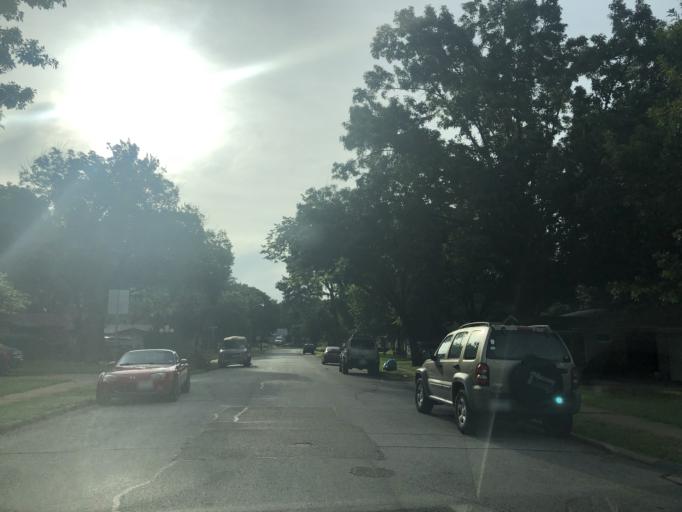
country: US
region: Texas
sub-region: Dallas County
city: Irving
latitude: 32.8048
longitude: -96.9738
